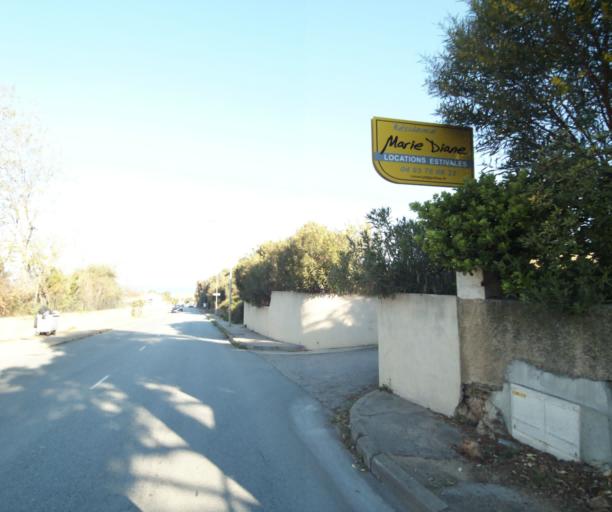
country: FR
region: Corsica
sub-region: Departement de la Corse-du-Sud
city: Propriano
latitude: 41.6711
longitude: 8.9122
